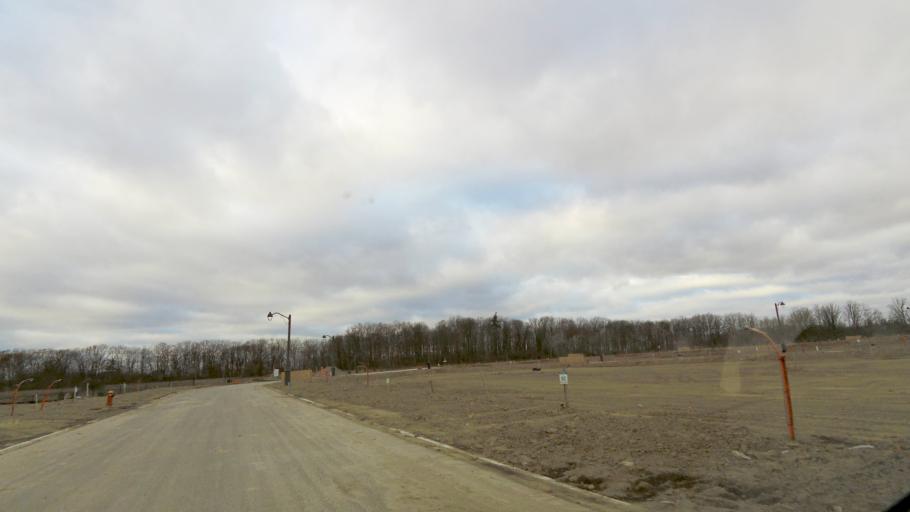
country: CA
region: Ontario
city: Oakville
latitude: 43.4968
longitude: -79.7224
